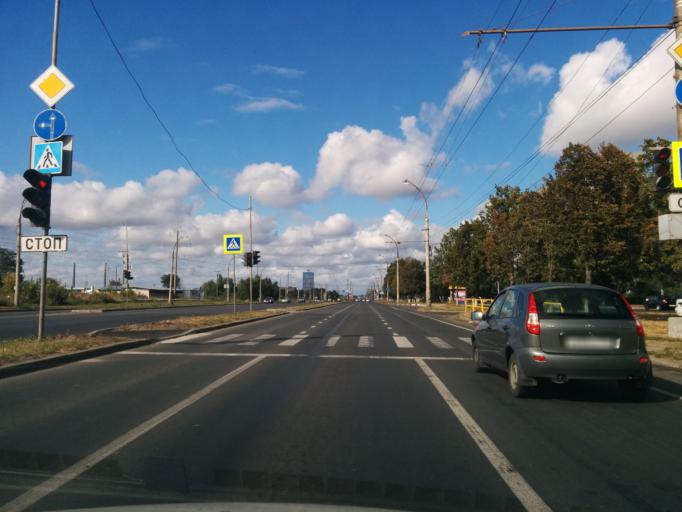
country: RU
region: Samara
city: Tol'yatti
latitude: 53.5365
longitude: 49.2633
